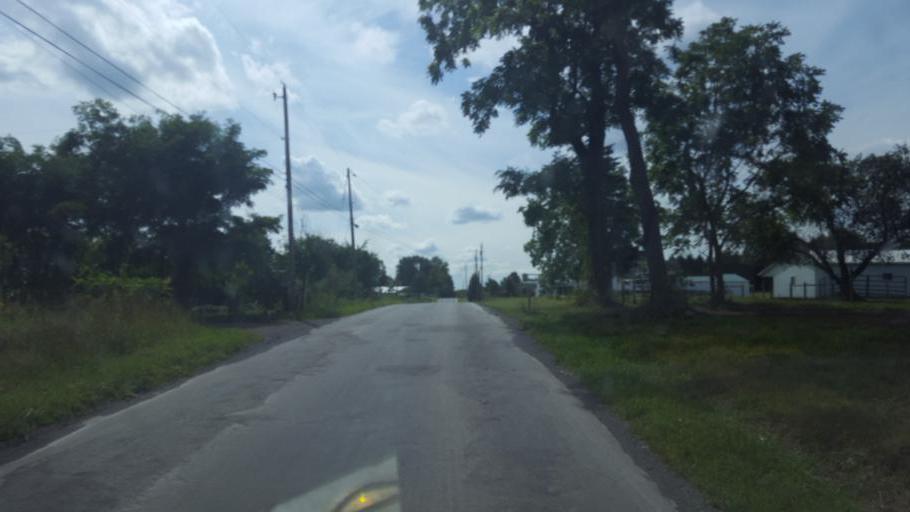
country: US
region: Ohio
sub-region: Geauga County
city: Middlefield
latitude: 41.4510
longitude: -80.9752
